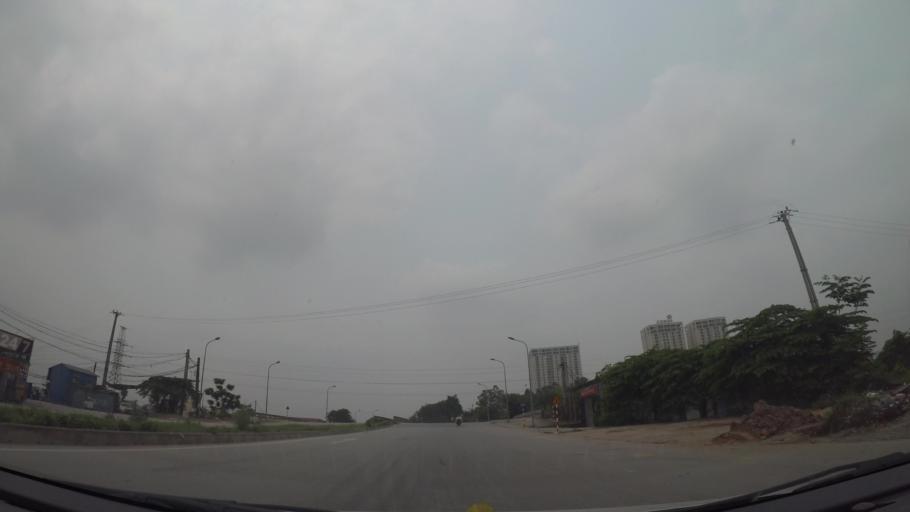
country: VN
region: Ha Noi
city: Cau Dien
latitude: 21.0123
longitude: 105.7467
